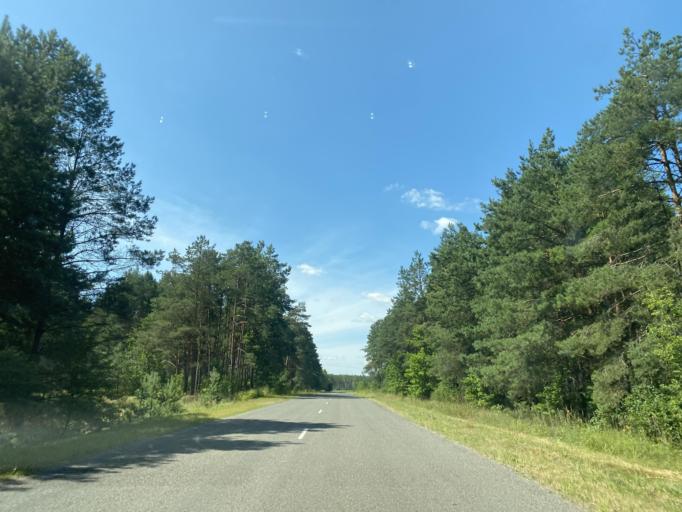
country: BY
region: Brest
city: Ivanava
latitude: 52.2245
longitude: 25.6352
